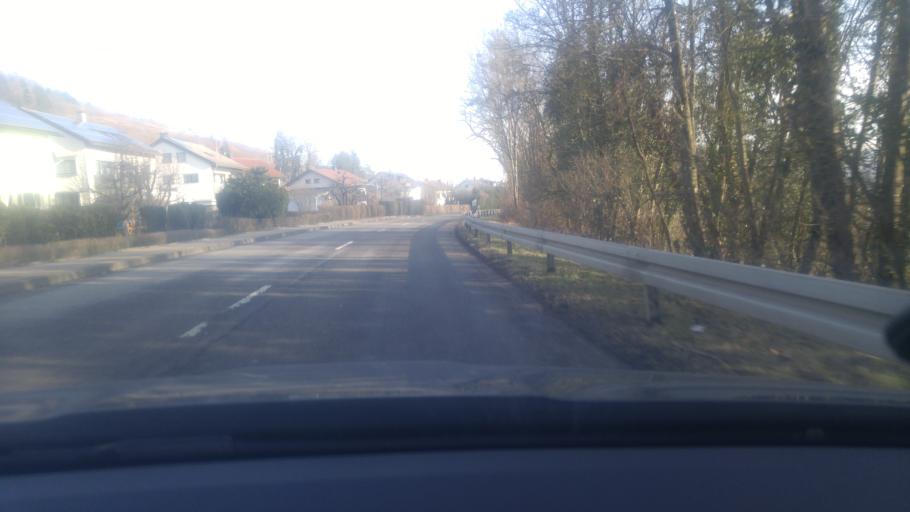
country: DE
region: Baden-Wuerttemberg
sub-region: Freiburg Region
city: Weilheim
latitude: 47.6446
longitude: 8.2500
